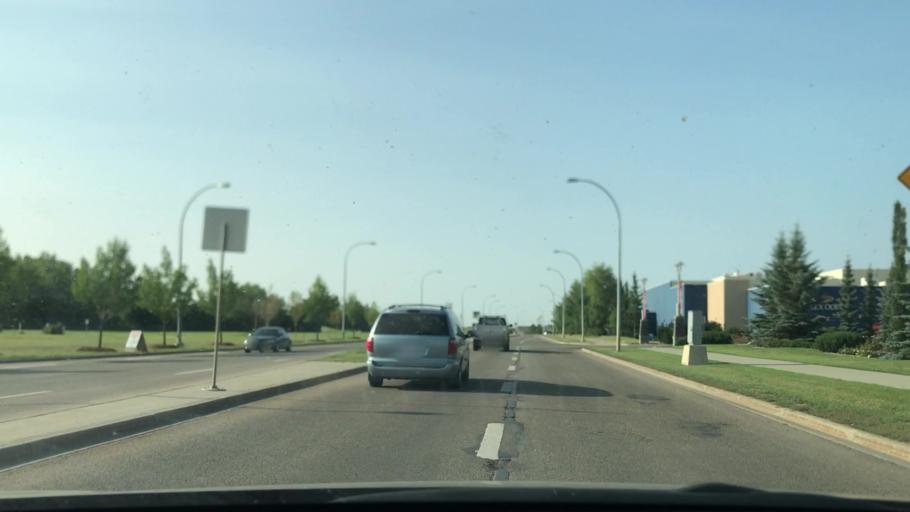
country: CA
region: Alberta
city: Edmonton
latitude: 53.4475
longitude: -113.4806
